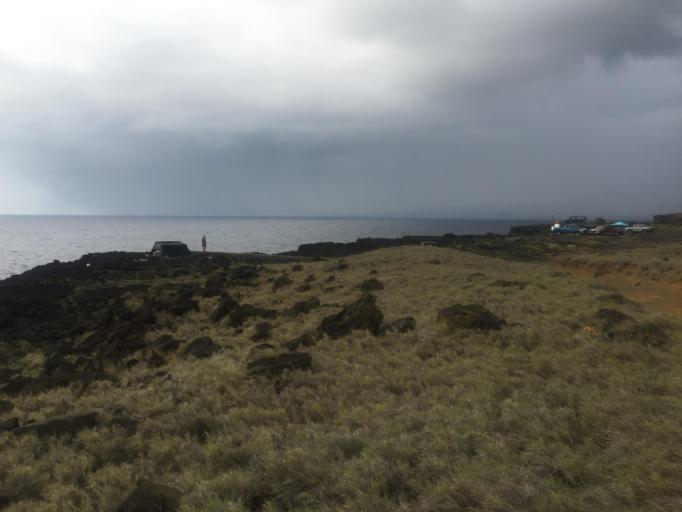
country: US
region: Hawaii
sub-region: Hawaii County
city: Hawaiian Ocean View
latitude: 18.9133
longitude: -155.6822
